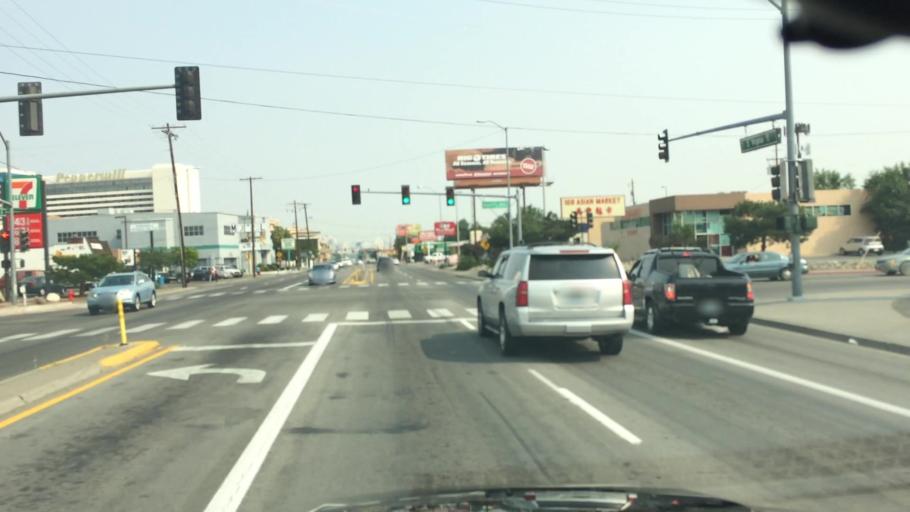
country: US
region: Nevada
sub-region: Washoe County
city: Reno
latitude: 39.4944
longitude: -119.7977
